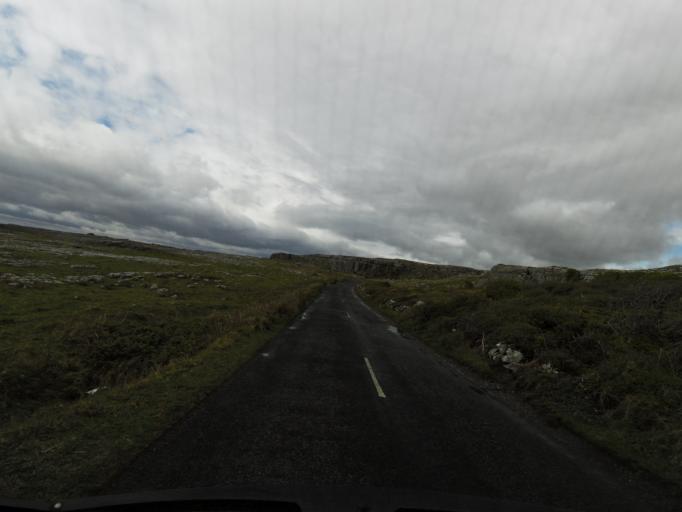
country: IE
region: Connaught
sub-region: County Galway
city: Bearna
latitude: 53.0637
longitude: -9.3603
